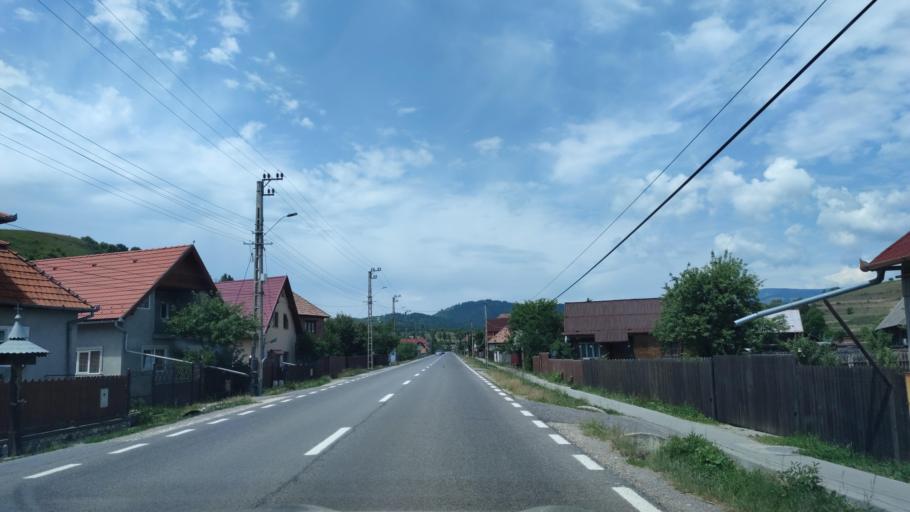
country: RO
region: Harghita
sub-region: Comuna Sandominic
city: Sandominic
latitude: 46.5914
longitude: 25.7670
